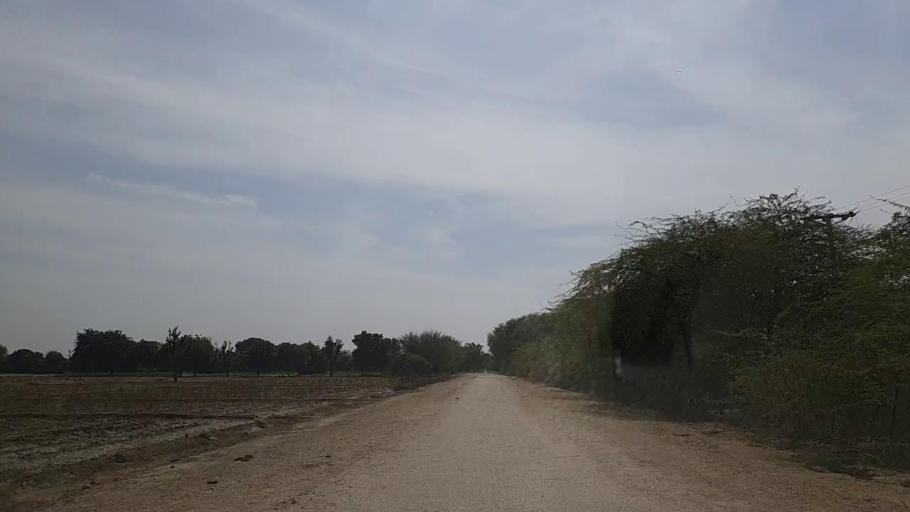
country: PK
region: Sindh
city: Samaro
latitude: 25.2329
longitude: 69.4733
